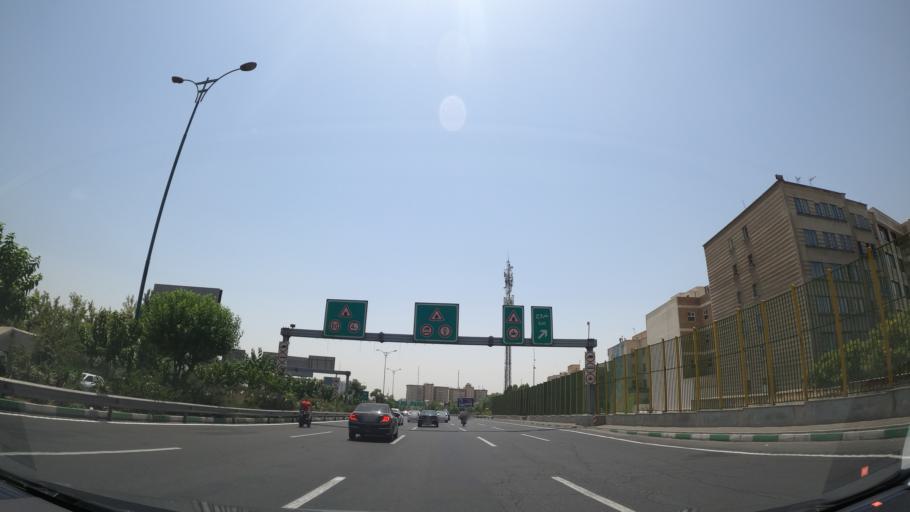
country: IR
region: Tehran
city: Tehran
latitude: 35.7196
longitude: 51.3783
